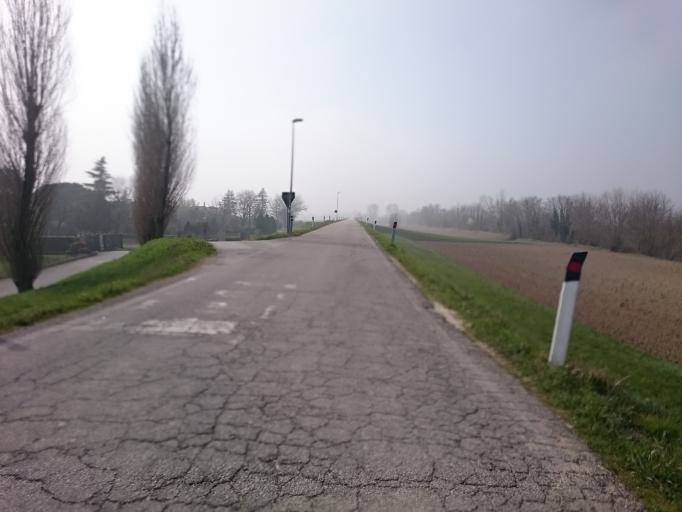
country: IT
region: Veneto
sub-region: Provincia di Padova
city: Due Carrare
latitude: 45.2821
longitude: 11.8325
